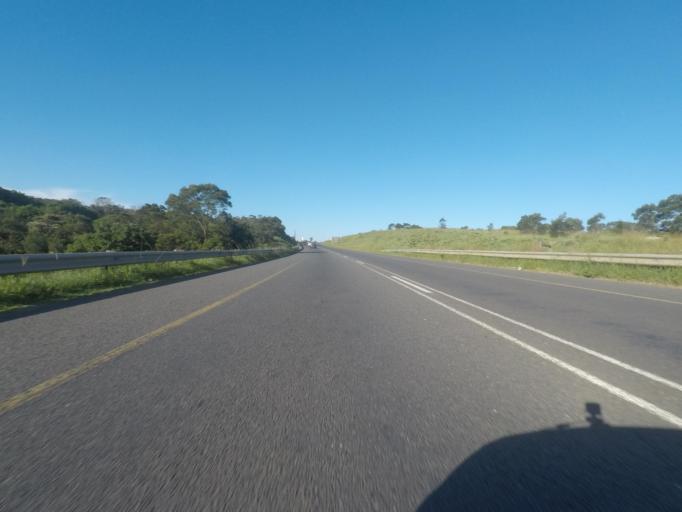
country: ZA
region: Eastern Cape
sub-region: Buffalo City Metropolitan Municipality
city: East London
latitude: -33.0430
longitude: 27.8288
